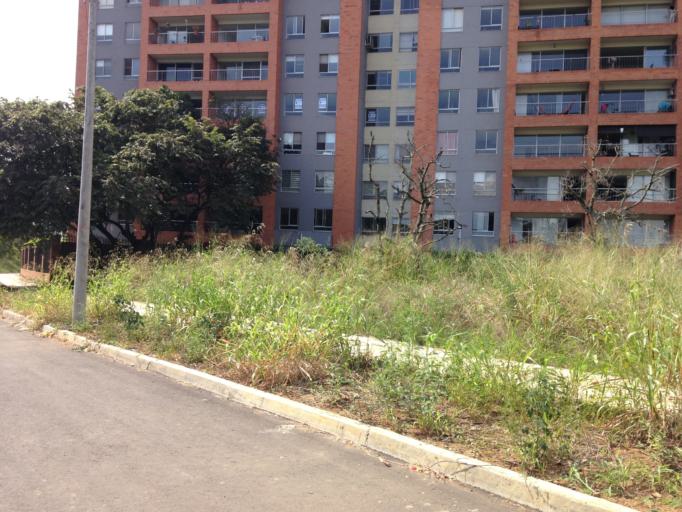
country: CO
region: Valle del Cauca
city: Cali
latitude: 3.3649
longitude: -76.5260
